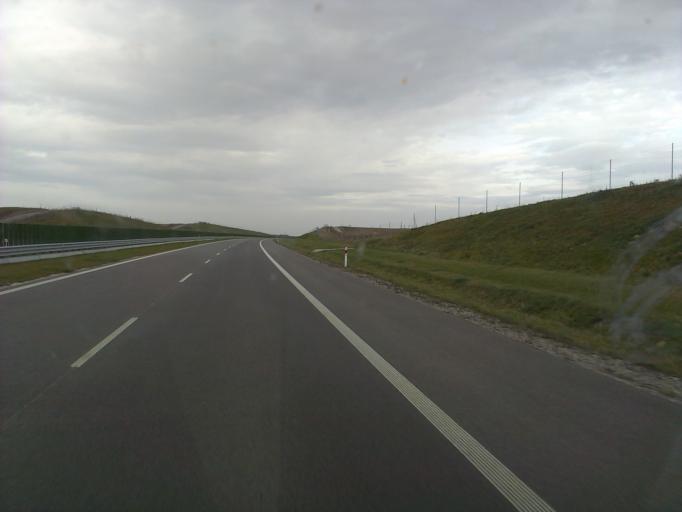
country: PL
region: Subcarpathian Voivodeship
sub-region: Powiat przeworski
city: Mirocin
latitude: 50.0284
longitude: 22.5763
